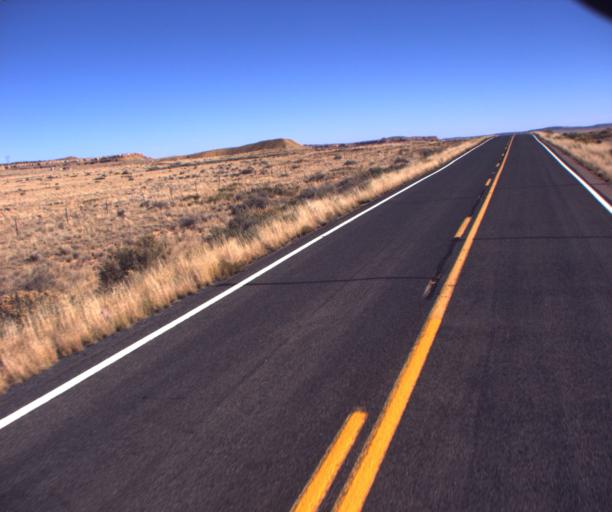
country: US
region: Arizona
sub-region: Navajo County
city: First Mesa
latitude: 35.9757
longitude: -110.7616
